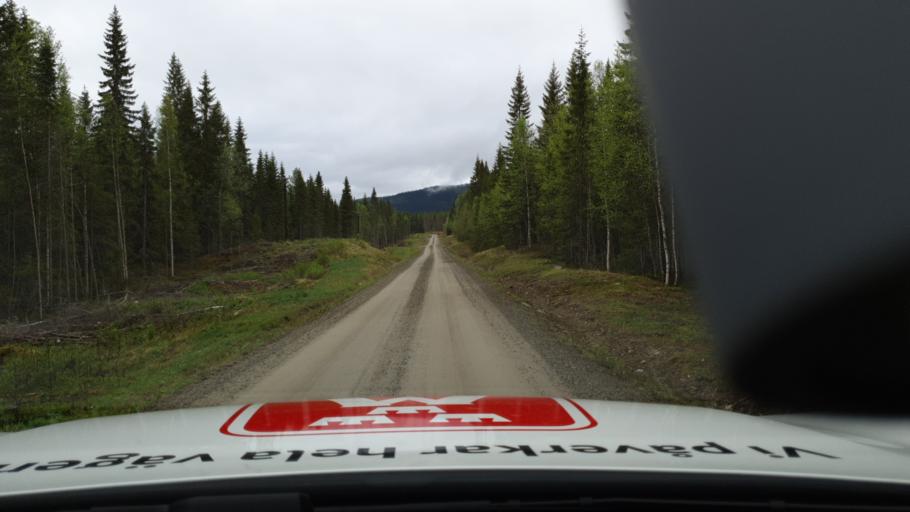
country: NO
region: Nord-Trondelag
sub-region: Lierne
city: Sandvika
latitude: 64.3988
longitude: 14.2937
